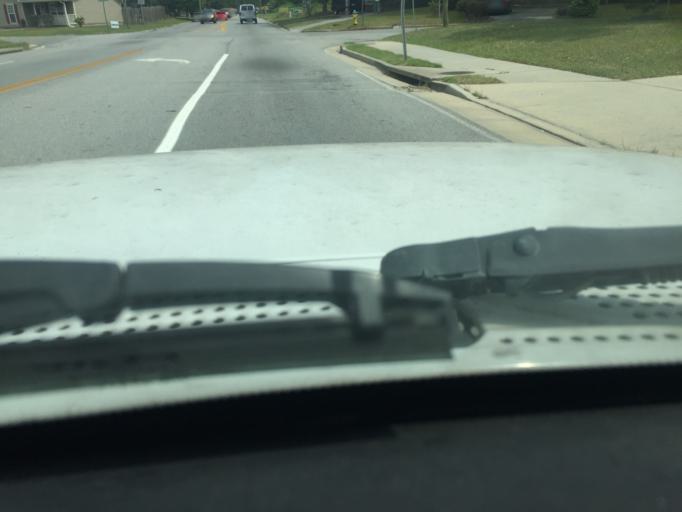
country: US
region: Georgia
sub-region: Chatham County
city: Isle of Hope
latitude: 31.9998
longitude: -81.0763
